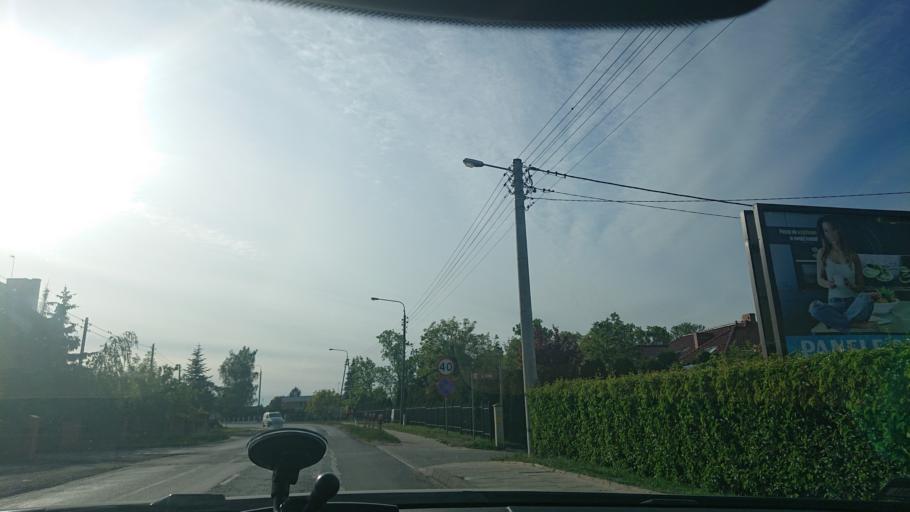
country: PL
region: Greater Poland Voivodeship
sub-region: Powiat gnieznienski
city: Gniezno
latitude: 52.5430
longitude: 17.5748
